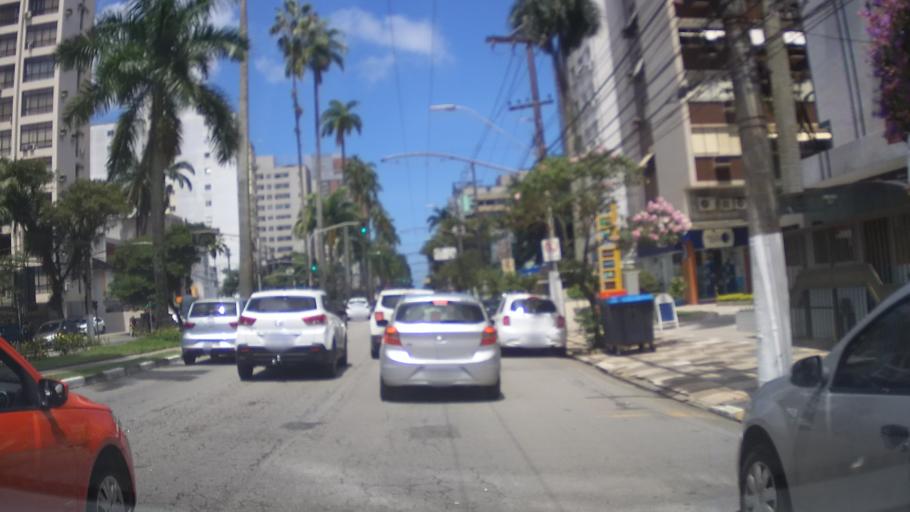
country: BR
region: Sao Paulo
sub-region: Santos
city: Santos
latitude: -23.9603
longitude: -46.3321
